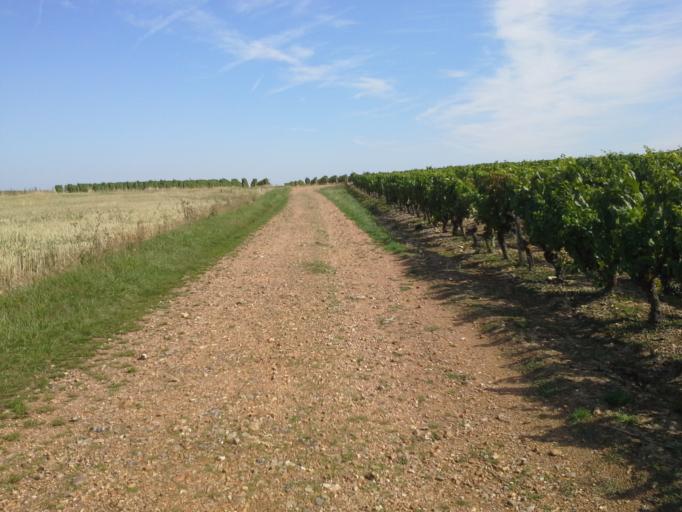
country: FR
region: Centre
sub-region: Departement du Loir-et-Cher
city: Villiers-sur-Loir
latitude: 47.8147
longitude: 0.9799
